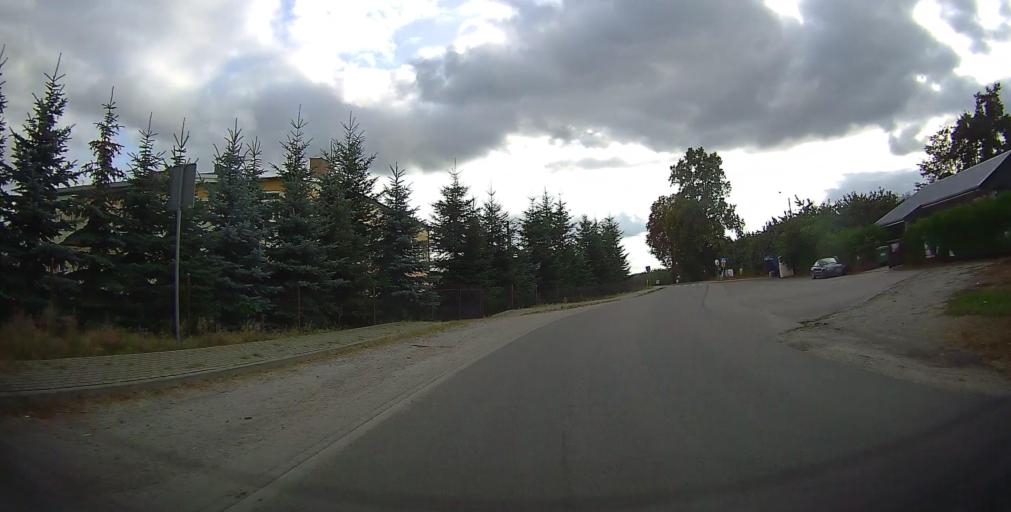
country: PL
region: Masovian Voivodeship
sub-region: Powiat bialobrzeski
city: Promna
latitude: 51.7301
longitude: 20.9644
